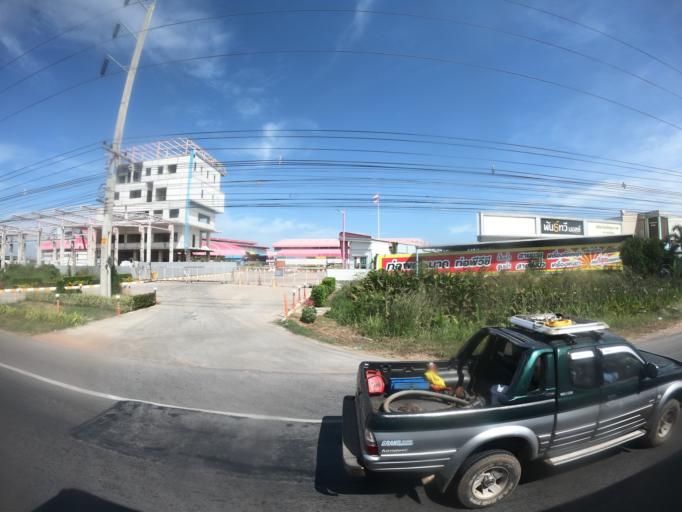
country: TH
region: Khon Kaen
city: Khon Kaen
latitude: 16.4377
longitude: 102.9245
